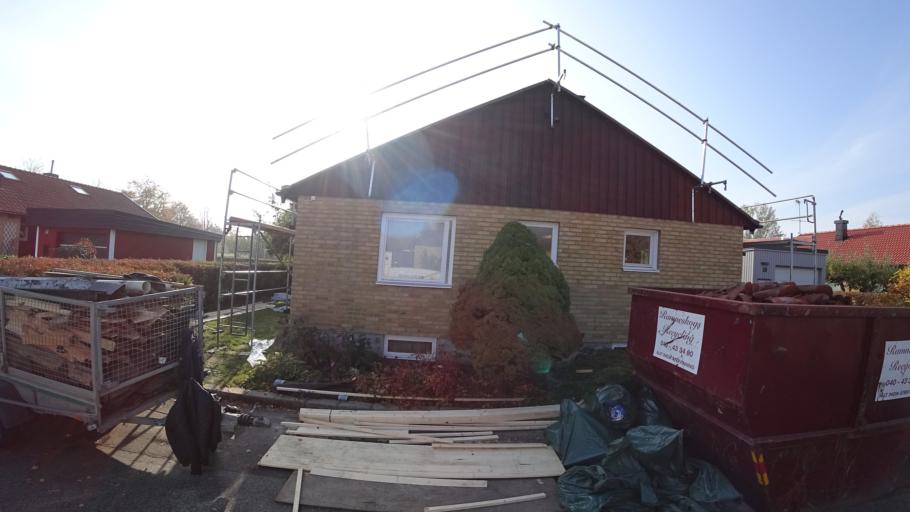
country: SE
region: Skane
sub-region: Staffanstorps Kommun
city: Staffanstorp
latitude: 55.6498
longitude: 13.2173
